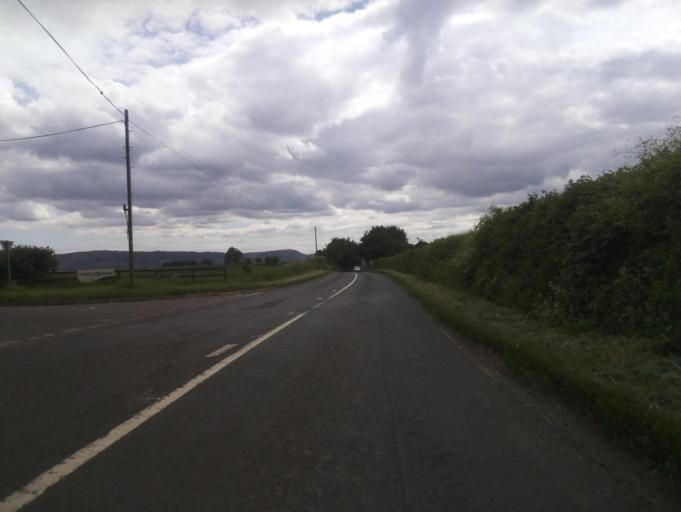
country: GB
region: England
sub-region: Herefordshire
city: Yatton
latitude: 51.9445
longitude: -2.5505
